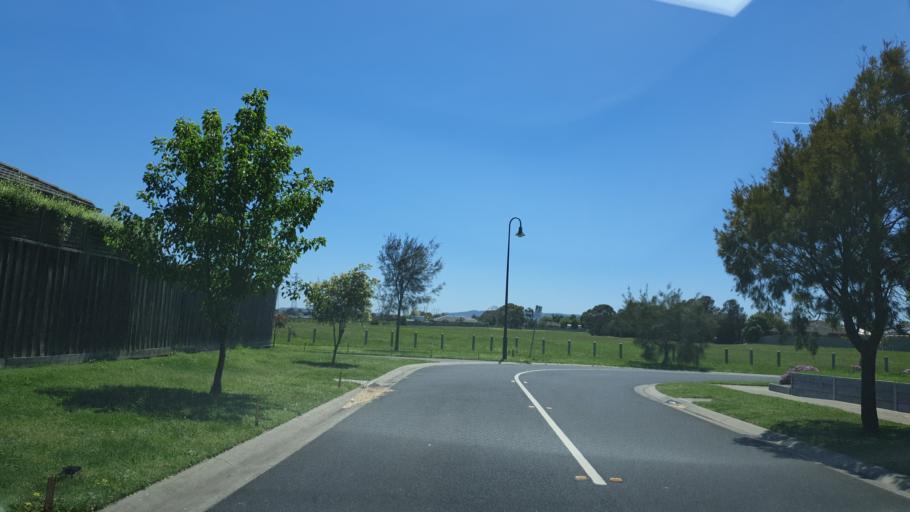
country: AU
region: Victoria
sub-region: Casey
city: Narre Warren South
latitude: -38.0600
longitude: 145.2818
